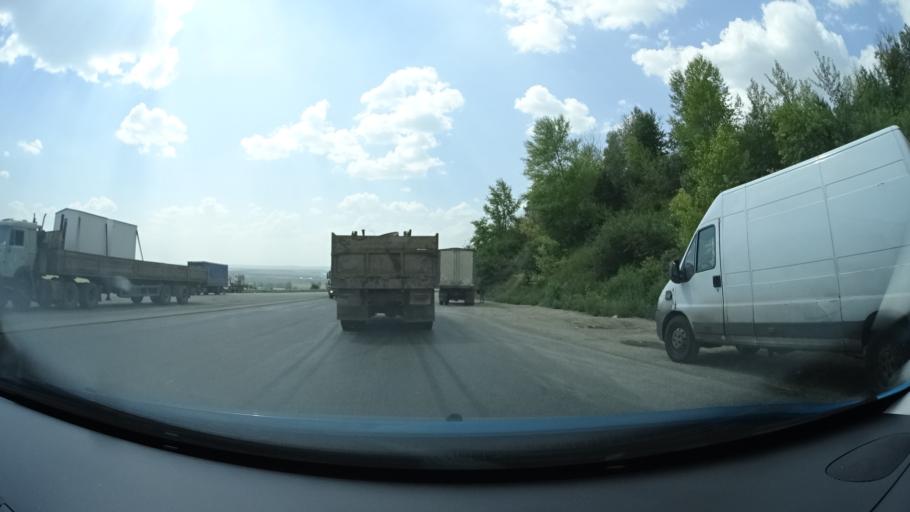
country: RU
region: Bashkortostan
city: Subkhankulovo
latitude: 54.5006
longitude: 53.9426
